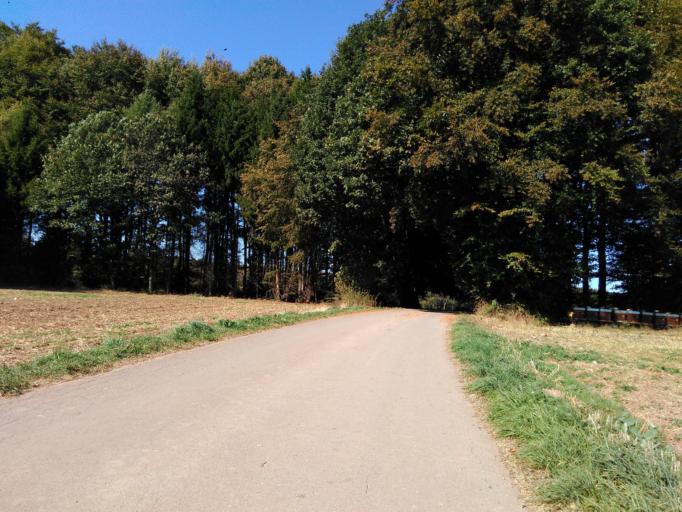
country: LU
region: Diekirch
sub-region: Canton de Redange
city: Rambrouch
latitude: 49.8098
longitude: 5.8436
